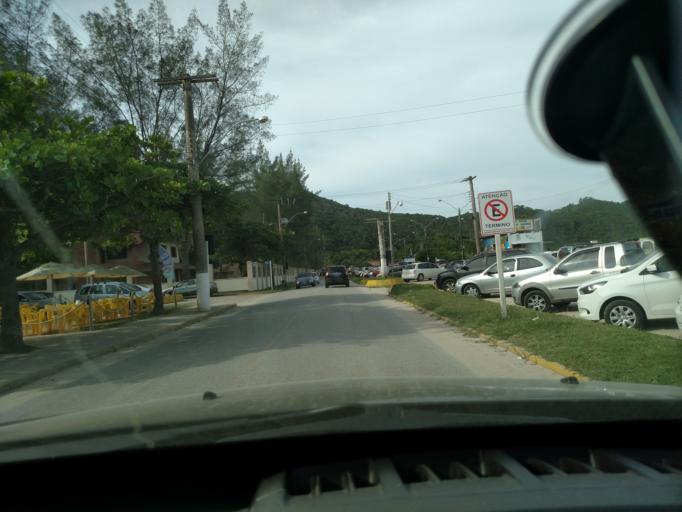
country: BR
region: Santa Catarina
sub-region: Porto Belo
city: Porto Belo
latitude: -27.1702
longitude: -48.4991
